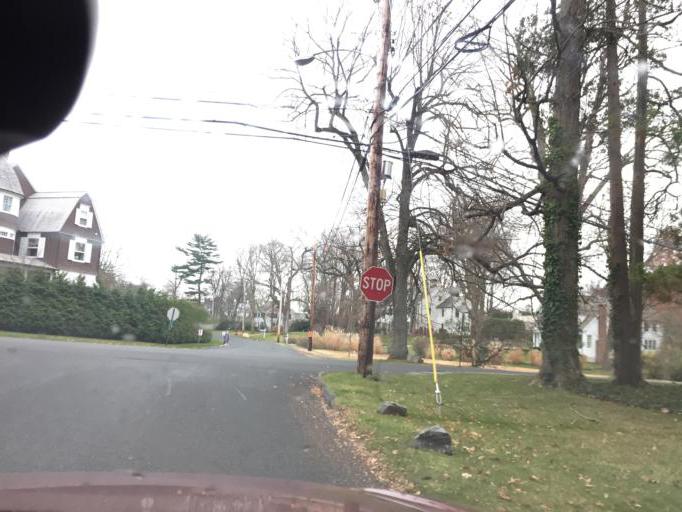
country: US
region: Connecticut
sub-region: Fairfield County
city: Southport
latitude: 41.1330
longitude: -73.2895
